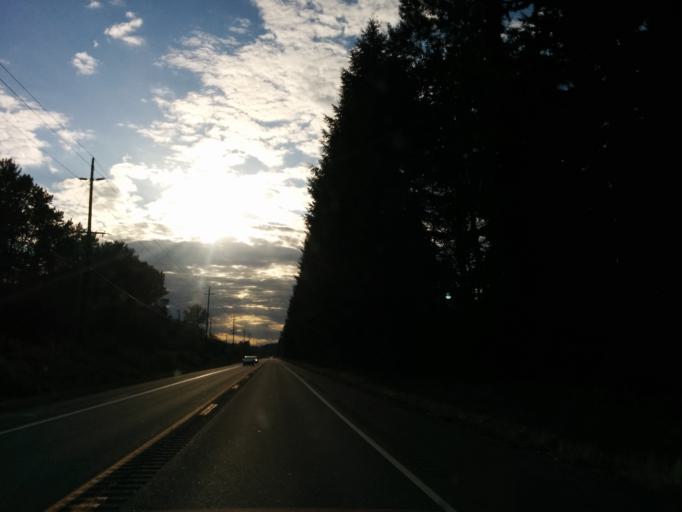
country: US
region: Washington
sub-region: Snohomish County
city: Woods Creek
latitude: 47.8549
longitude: -121.9075
